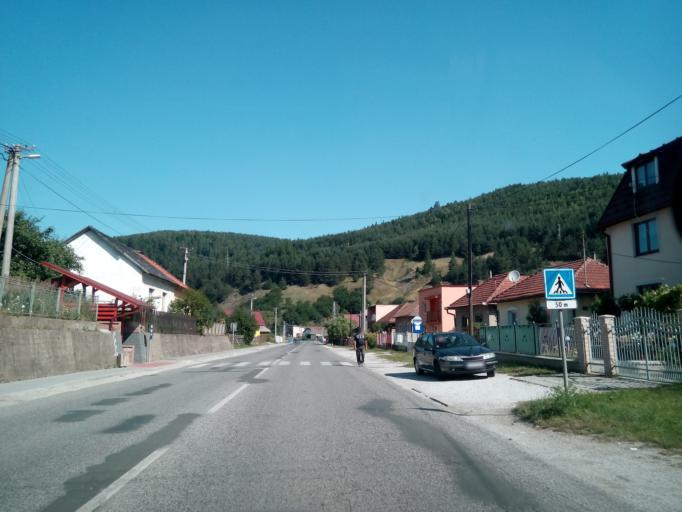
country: SK
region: Kosicky
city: Krompachy
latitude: 48.9253
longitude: 20.8578
